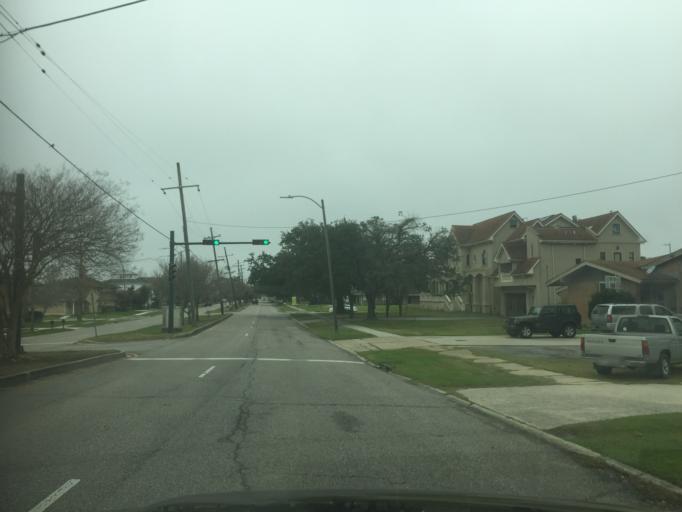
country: US
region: Louisiana
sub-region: Jefferson Parish
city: Metairie
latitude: 30.0189
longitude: -90.0987
